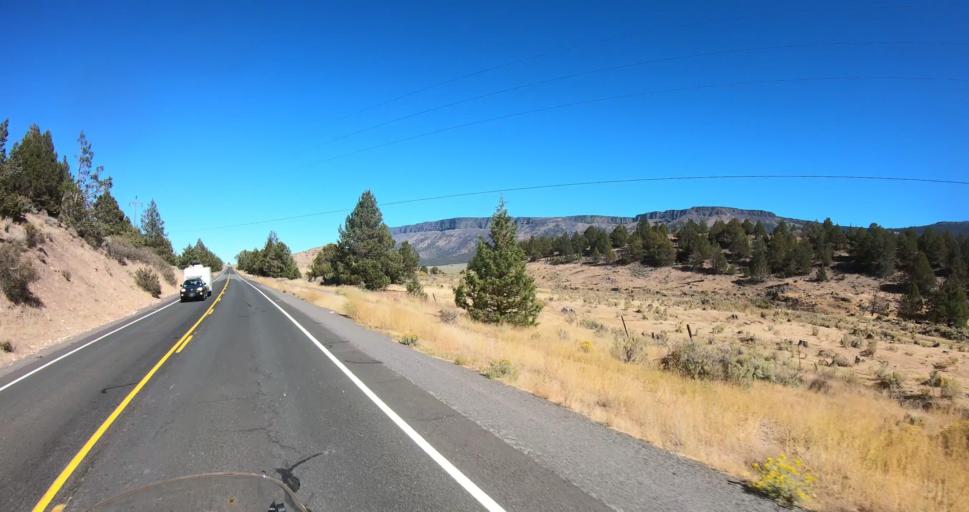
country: US
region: Oregon
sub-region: Lake County
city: Lakeview
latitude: 42.4304
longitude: -120.2824
